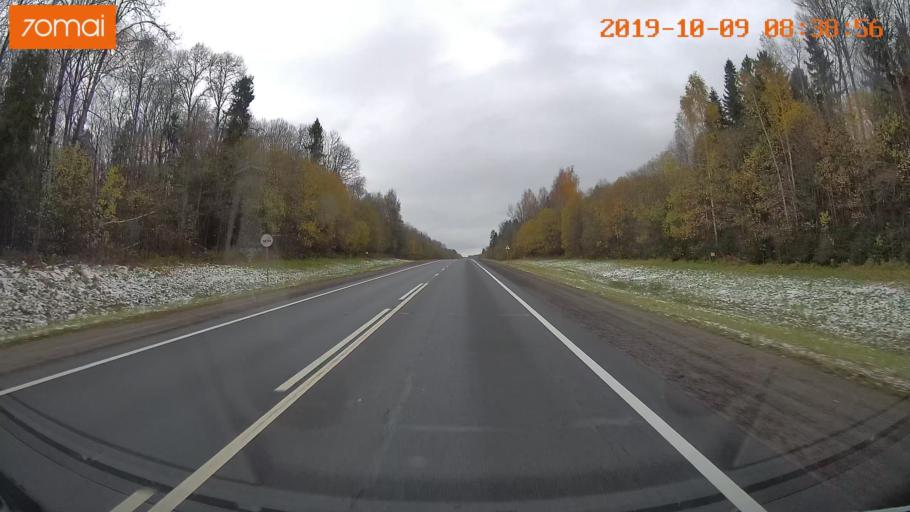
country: RU
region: Vologda
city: Gryazovets
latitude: 58.9640
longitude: 40.1594
